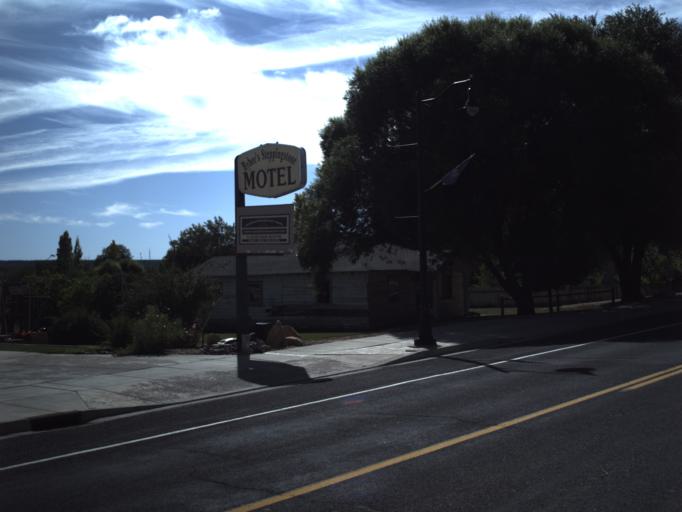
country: US
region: Utah
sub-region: Garfield County
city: Panguitch
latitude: 37.6236
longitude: -112.0818
